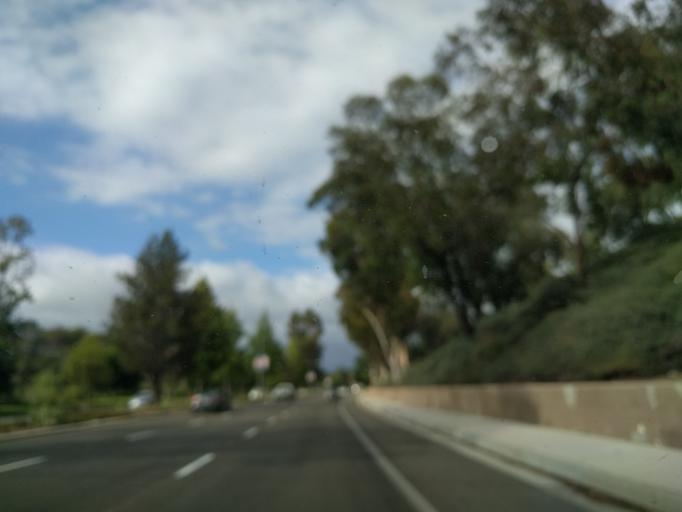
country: US
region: California
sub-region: Orange County
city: Laguna Niguel
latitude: 33.5469
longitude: -117.6897
